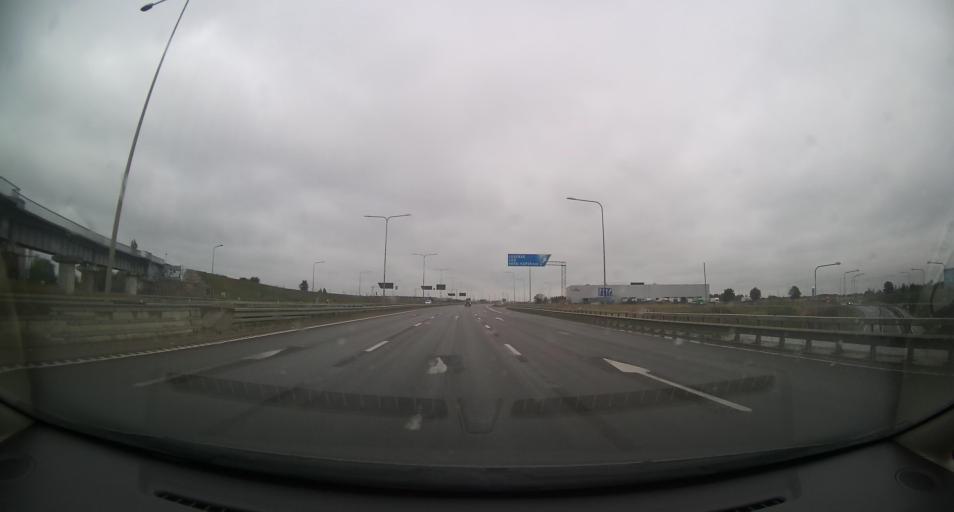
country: EE
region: Harju
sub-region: Joelaehtme vald
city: Loo
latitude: 59.4413
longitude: 24.9293
